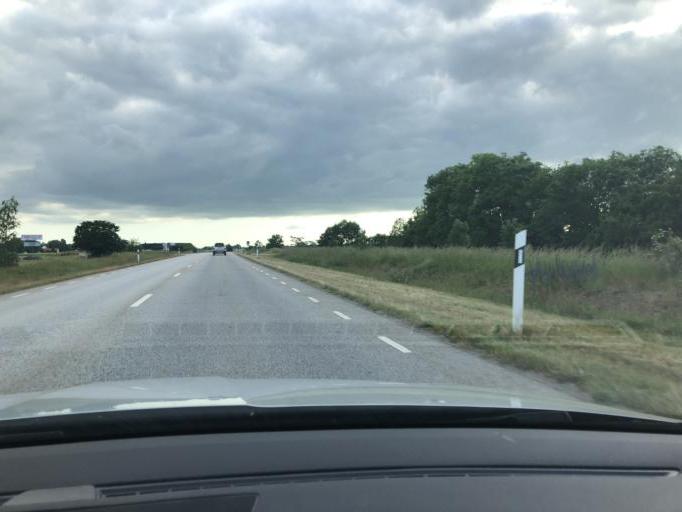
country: SE
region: Skane
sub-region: Simrishamns Kommun
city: Simrishamn
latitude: 55.5433
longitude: 14.3338
